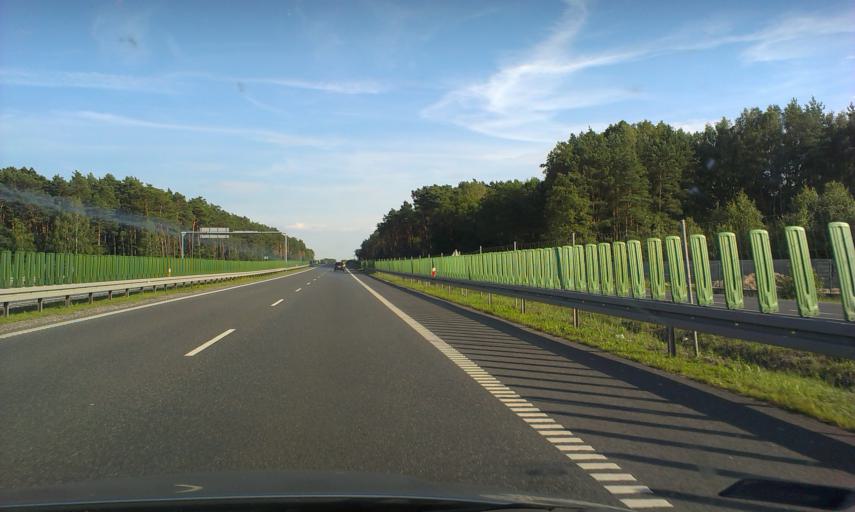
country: PL
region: Kujawsko-Pomorskie
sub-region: Powiat bydgoski
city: Biale Blota
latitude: 53.0849
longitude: 17.9058
